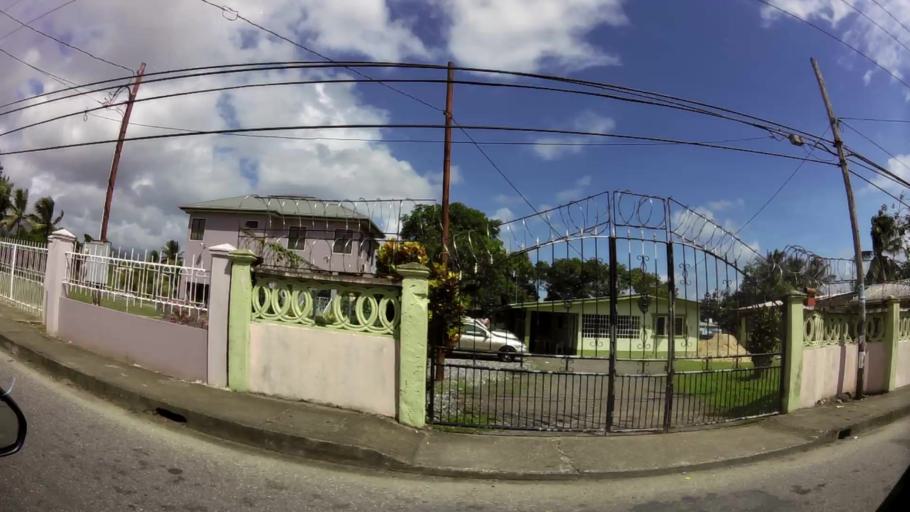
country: TT
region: Borough of Arima
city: Arima
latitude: 10.6249
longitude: -61.2665
